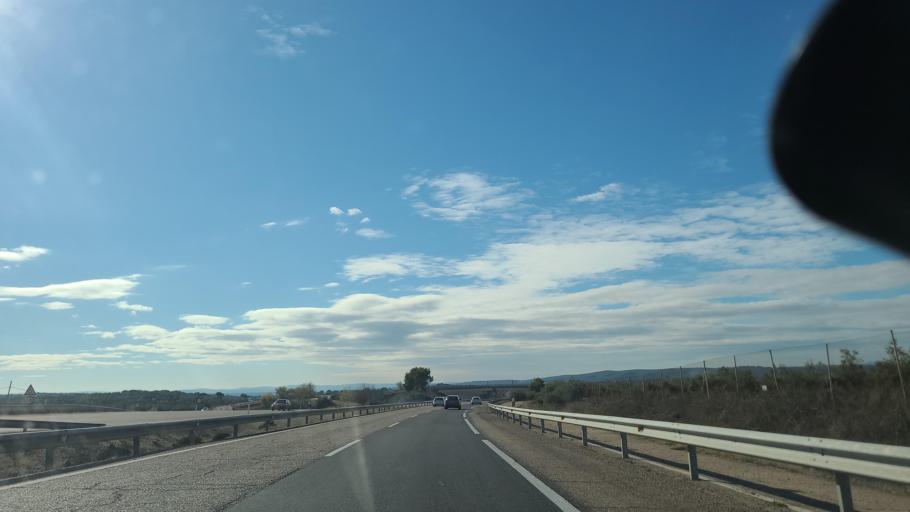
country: ES
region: Andalusia
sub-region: Provincia de Jaen
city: Bailen
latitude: 38.0916
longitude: -3.8151
